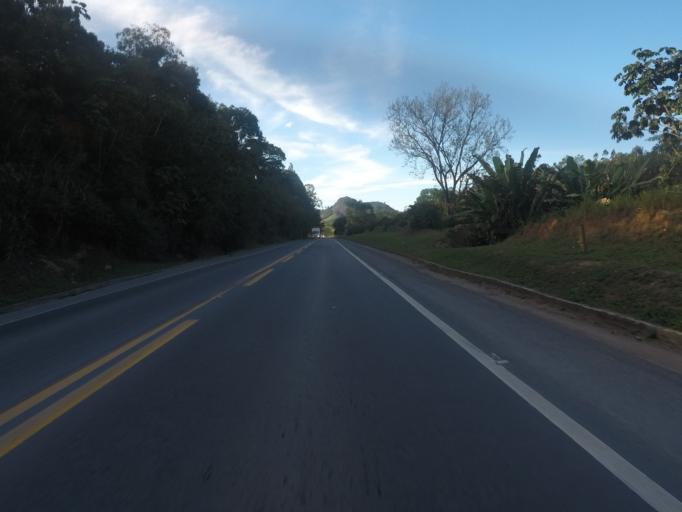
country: BR
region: Espirito Santo
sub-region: Fundao
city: Fundao
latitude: -19.8778
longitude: -40.4159
